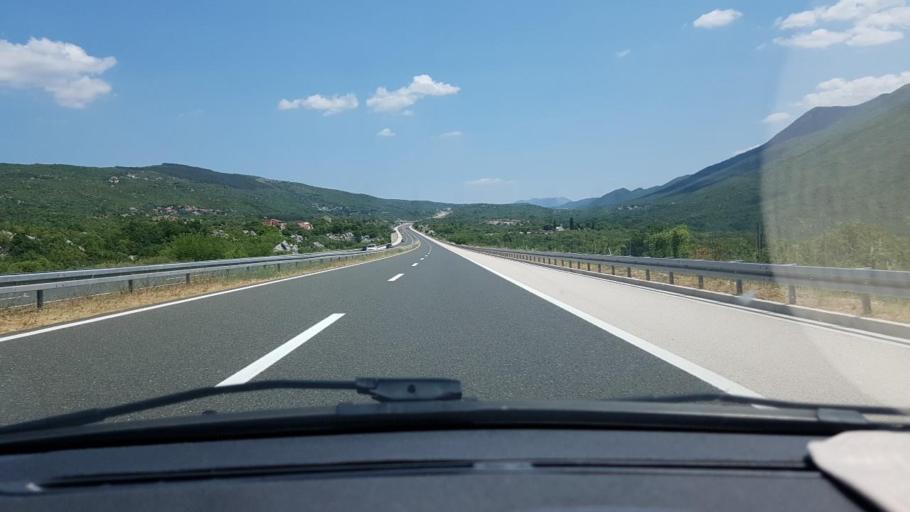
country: HR
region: Splitsko-Dalmatinska
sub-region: Grad Makarska
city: Makarska
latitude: 43.3932
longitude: 17.0471
